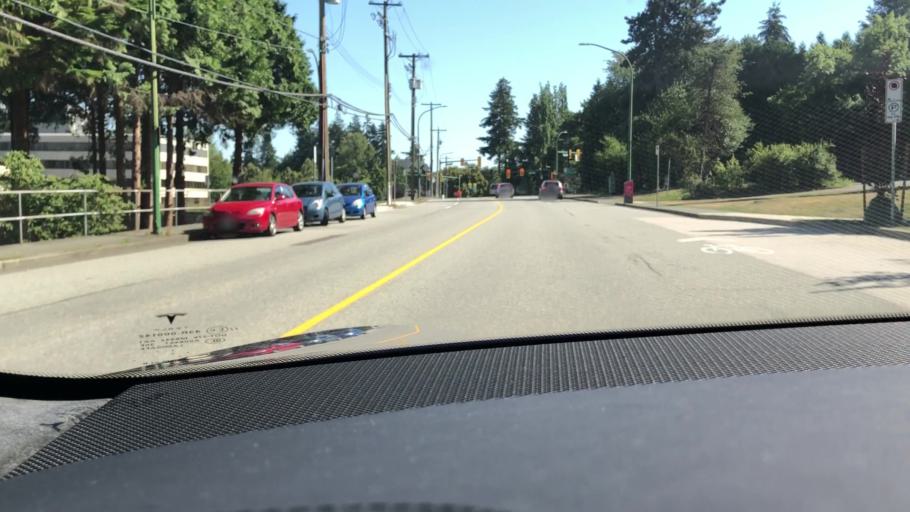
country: CA
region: British Columbia
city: Burnaby
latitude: 49.2469
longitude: -122.9747
